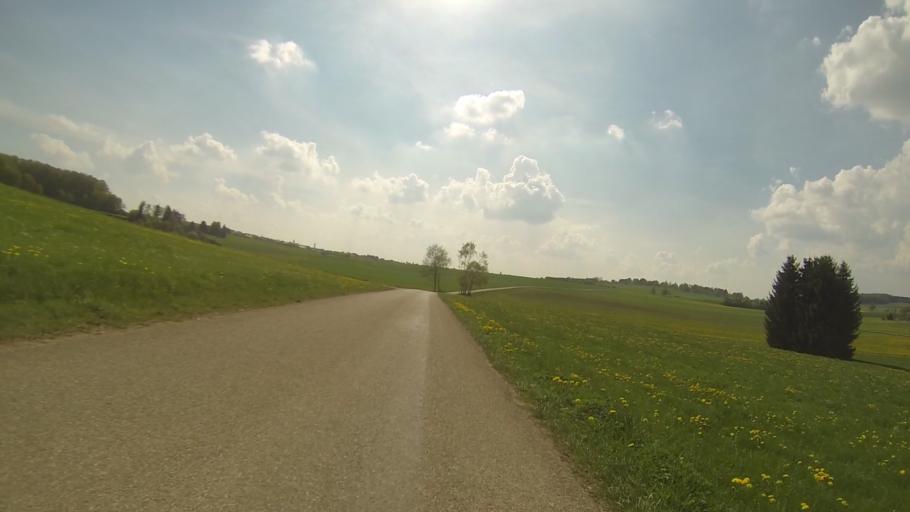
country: DE
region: Baden-Wuerttemberg
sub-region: Regierungsbezirk Stuttgart
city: Gerstetten
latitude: 48.6346
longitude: 10.0382
